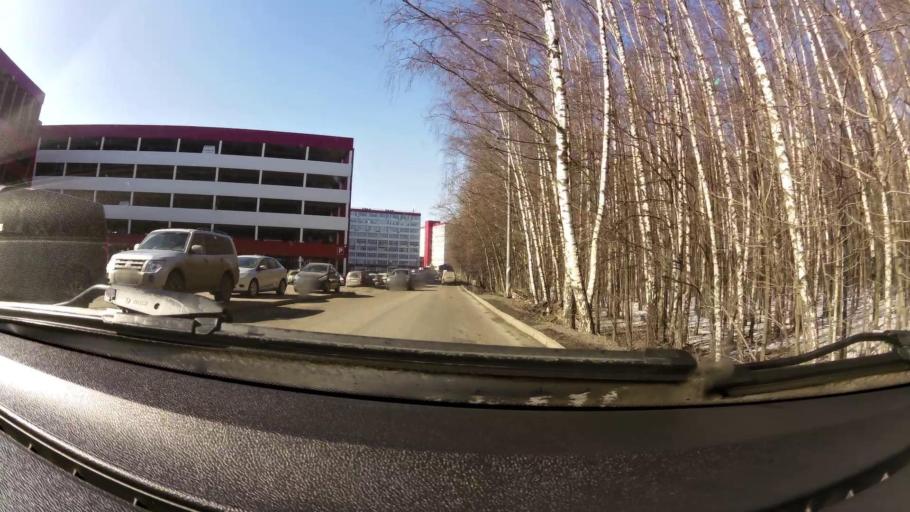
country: RU
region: Moskovskaya
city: Mosrentgen
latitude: 55.6347
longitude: 37.4453
